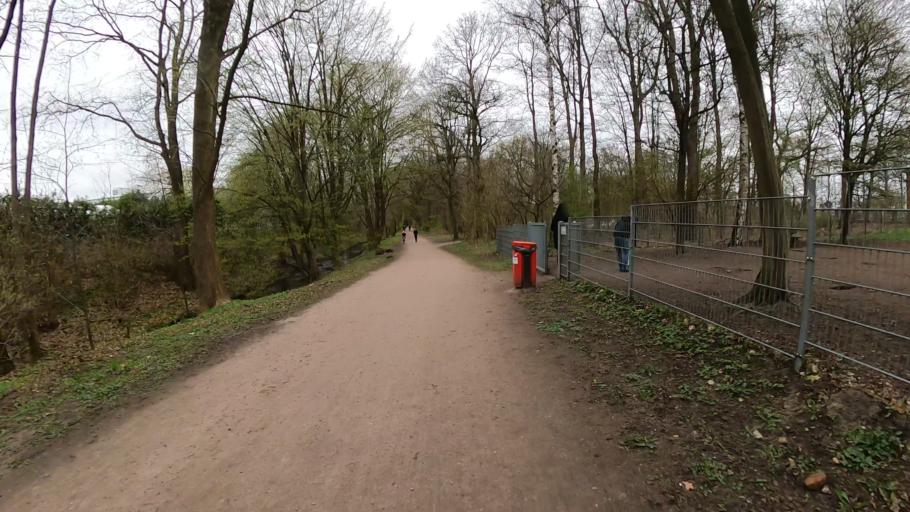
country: DE
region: Hamburg
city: Langenhorn
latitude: 53.6663
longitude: 9.9914
